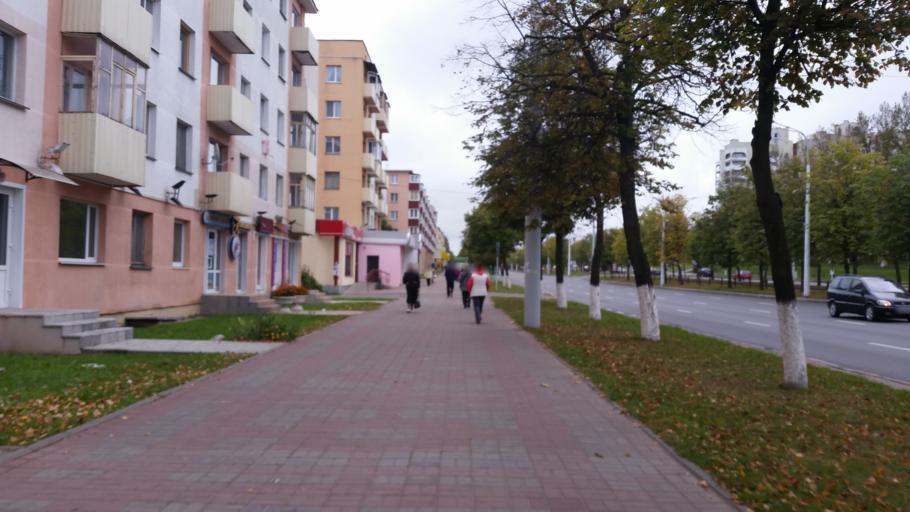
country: BY
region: Vitebsk
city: Vitebsk
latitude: 55.1814
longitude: 30.2118
